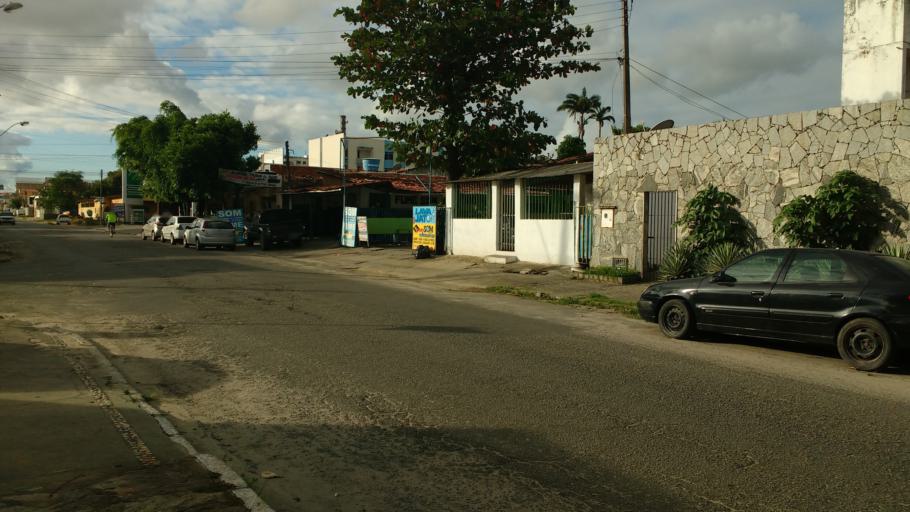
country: BR
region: Alagoas
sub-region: Maceio
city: Maceio
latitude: -9.6326
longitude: -35.7398
